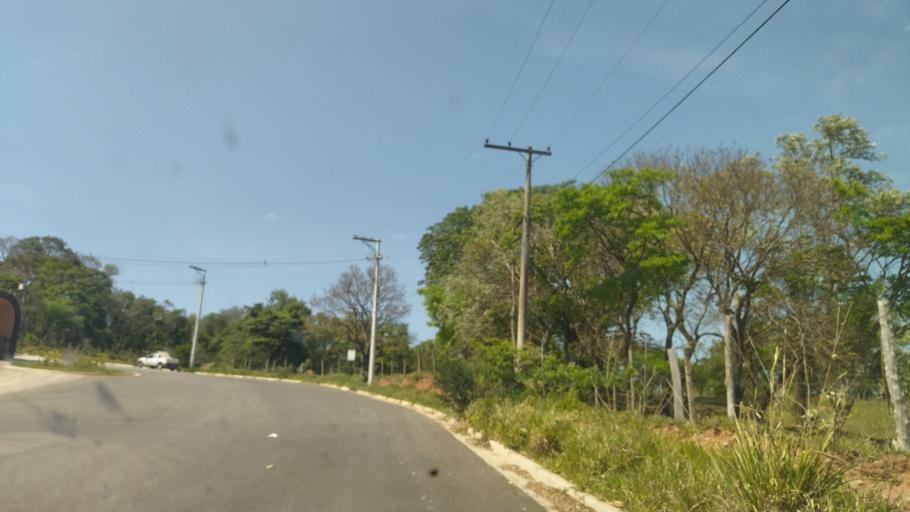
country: BR
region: Sao Paulo
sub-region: Atibaia
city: Atibaia
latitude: -23.1318
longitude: -46.5445
